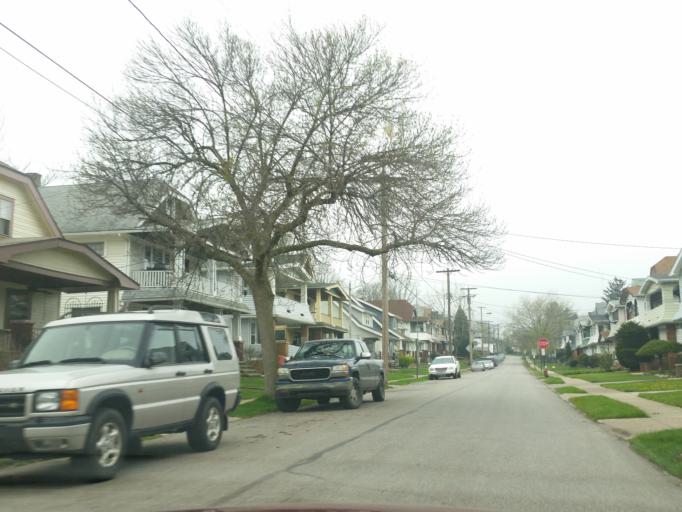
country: US
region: Ohio
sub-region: Cuyahoga County
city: Brooklyn Heights
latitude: 41.4333
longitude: -81.6995
